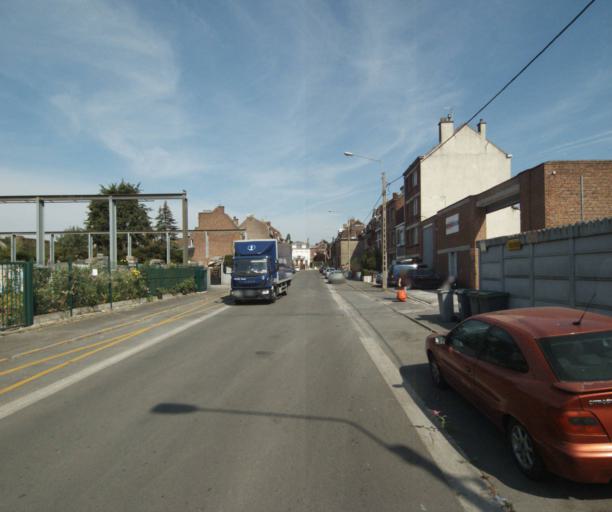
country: FR
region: Nord-Pas-de-Calais
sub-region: Departement du Nord
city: Mouvaux
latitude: 50.7135
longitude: 3.1361
